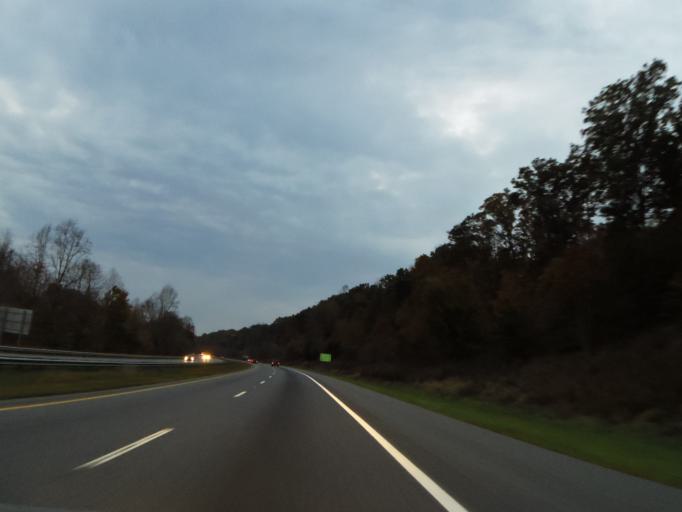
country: US
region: North Carolina
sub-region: McDowell County
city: Marion
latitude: 35.6815
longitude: -81.9376
